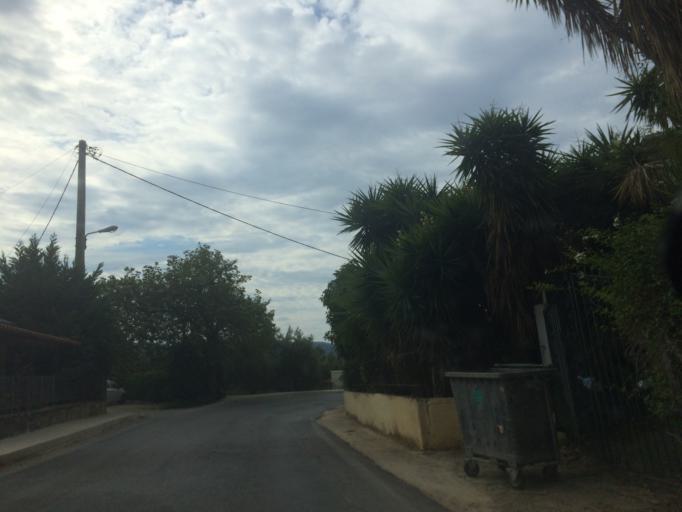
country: GR
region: Peloponnese
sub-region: Nomos Messinias
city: Pylos
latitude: 36.9534
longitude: 21.7033
